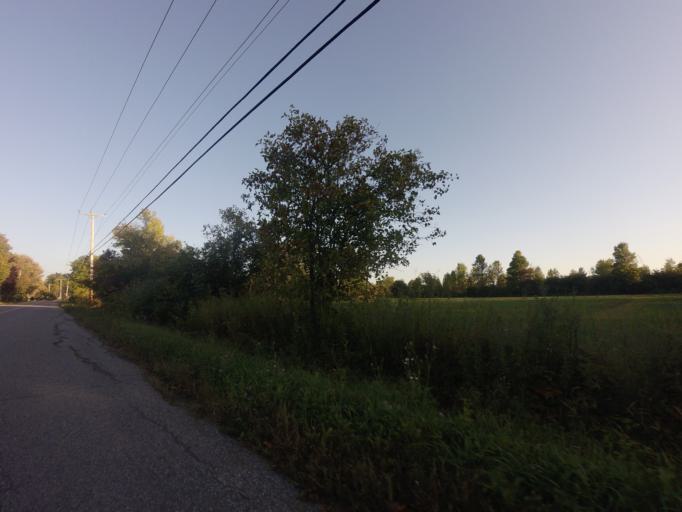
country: CA
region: Quebec
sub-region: Monteregie
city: Rigaud
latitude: 45.4793
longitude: -74.2426
